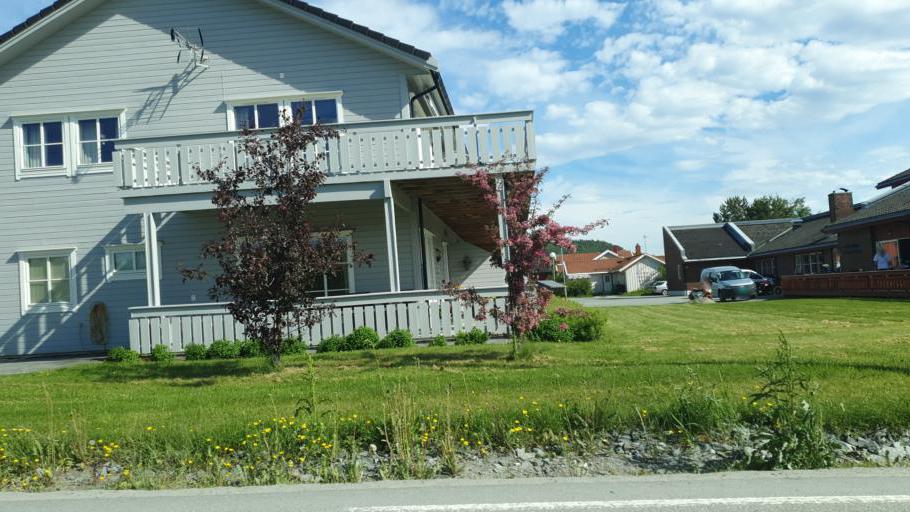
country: NO
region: Sor-Trondelag
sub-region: Rissa
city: Rissa
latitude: 63.5082
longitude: 10.0173
